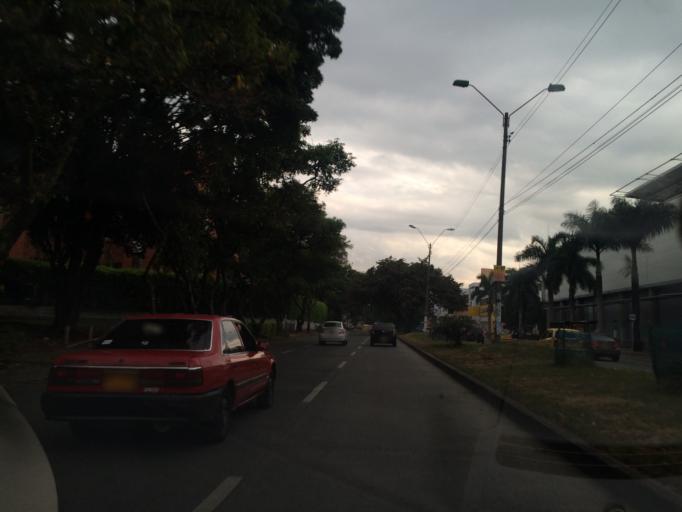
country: CO
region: Valle del Cauca
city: Cali
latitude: 3.4125
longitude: -76.5413
